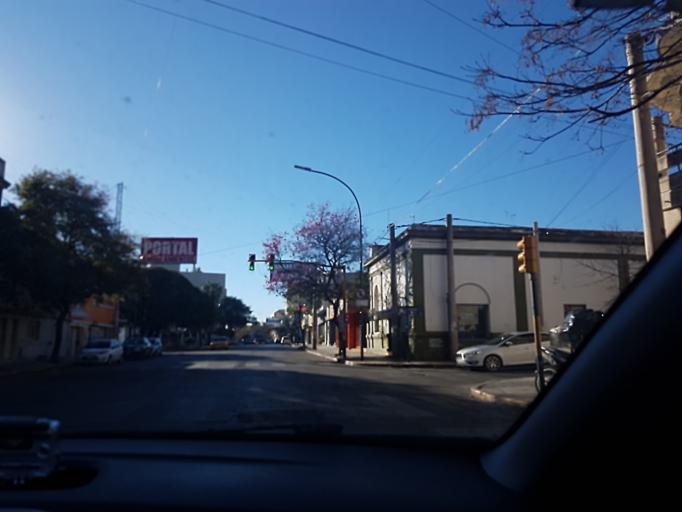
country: AR
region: Cordoba
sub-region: Departamento de Capital
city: Cordoba
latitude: -31.4035
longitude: -64.1951
